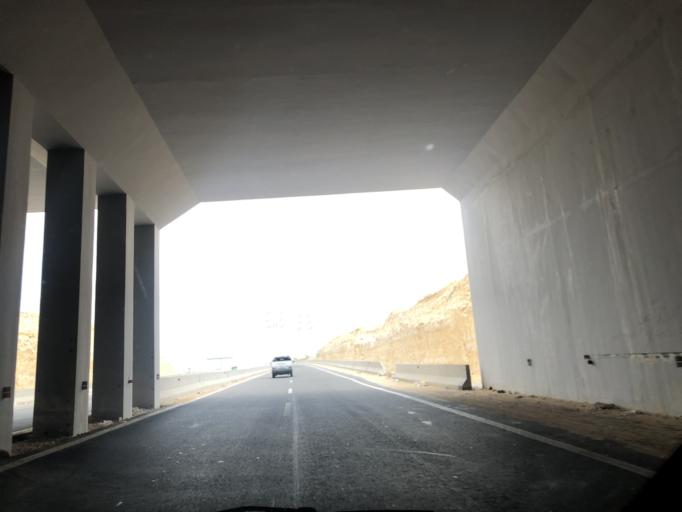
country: EG
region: Muhafazat al Qahirah
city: Halwan
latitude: 29.9114
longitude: 31.4612
